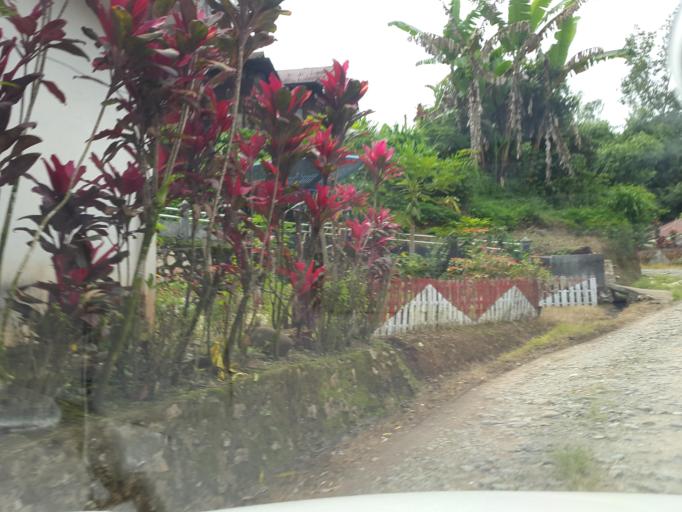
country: ID
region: South Sulawesi
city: Rantepang
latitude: -2.8713
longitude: 119.9463
